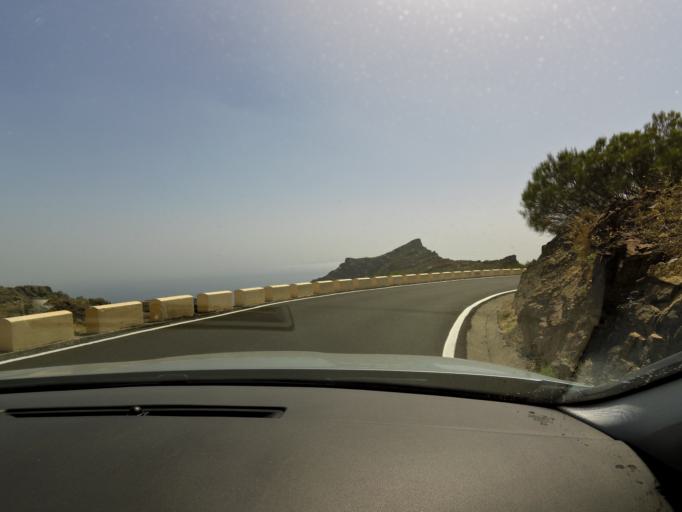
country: ES
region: Canary Islands
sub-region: Provincia de Santa Cruz de Tenerife
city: Santiago del Teide
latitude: 28.2992
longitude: -16.8273
